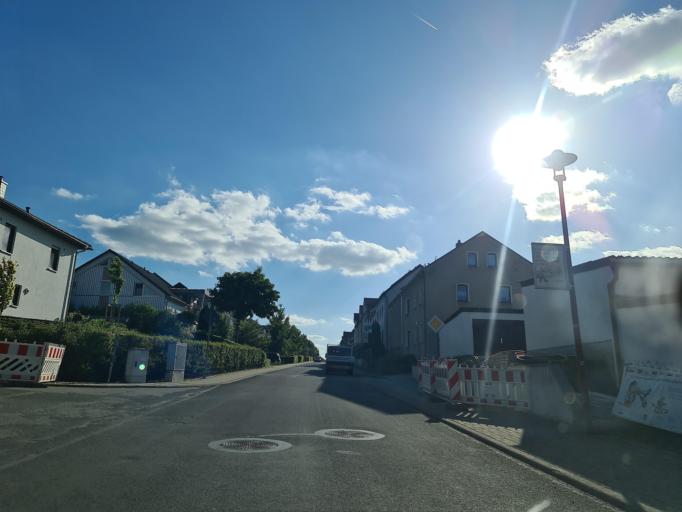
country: DE
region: Saxony
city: Weischlitz
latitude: 50.4916
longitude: 12.0869
